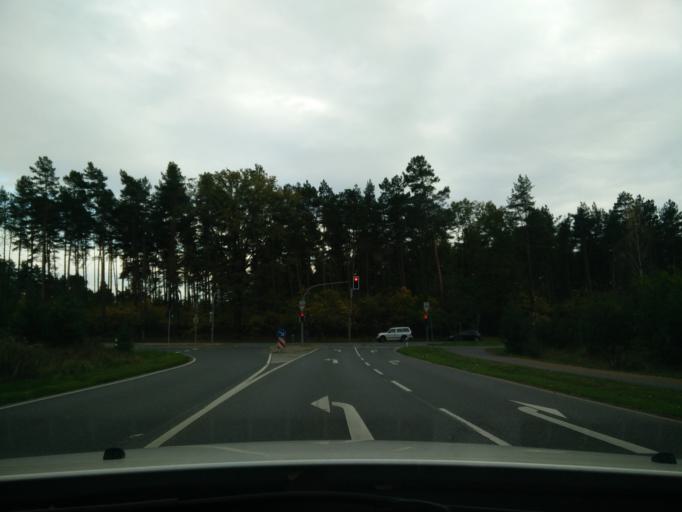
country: DE
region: Brandenburg
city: Hennigsdorf
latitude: 52.6716
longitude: 13.2072
